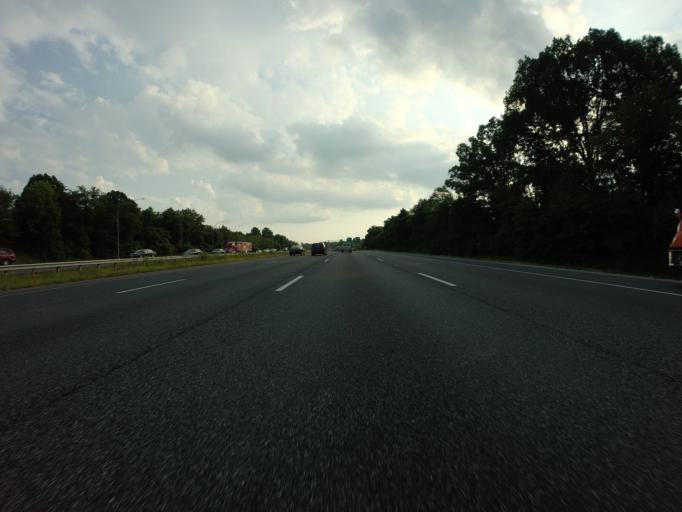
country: US
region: Maryland
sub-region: Howard County
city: West Elkridge
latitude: 39.2018
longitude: -76.7597
